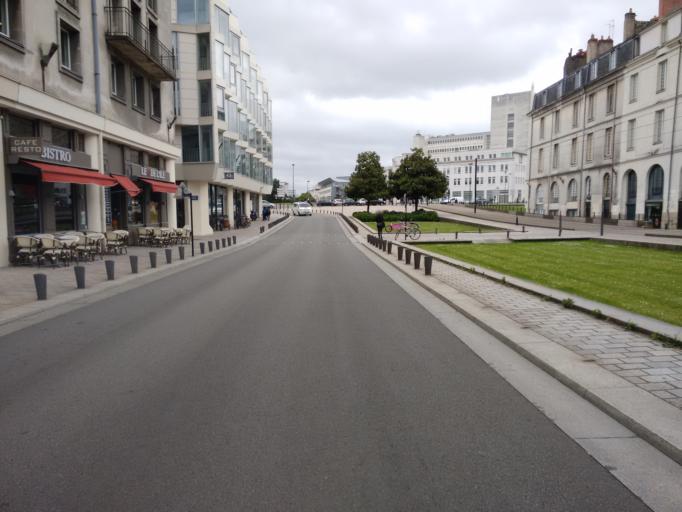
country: FR
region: Pays de la Loire
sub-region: Departement de la Loire-Atlantique
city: Nantes
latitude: 47.2136
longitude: -1.5547
